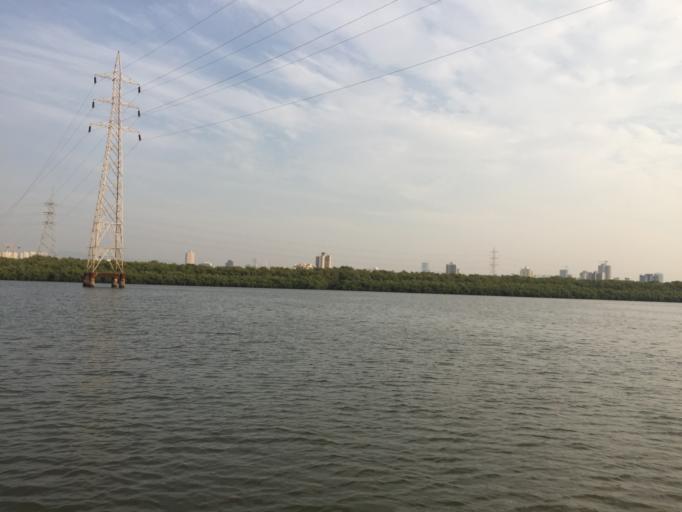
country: IN
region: Maharashtra
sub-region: Mumbai Suburban
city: Borivli
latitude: 19.2278
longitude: 72.8155
